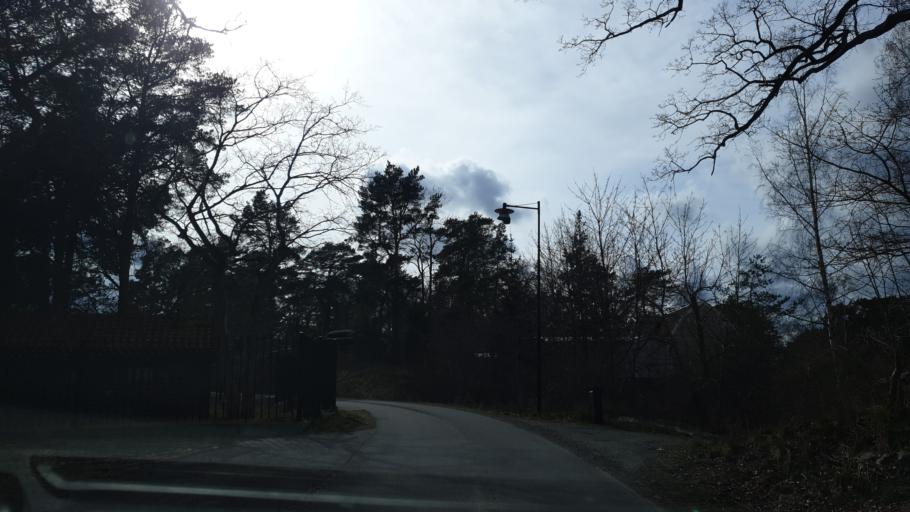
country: SE
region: Stockholm
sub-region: Tyreso Kommun
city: Brevik
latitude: 59.2650
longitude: 18.3600
